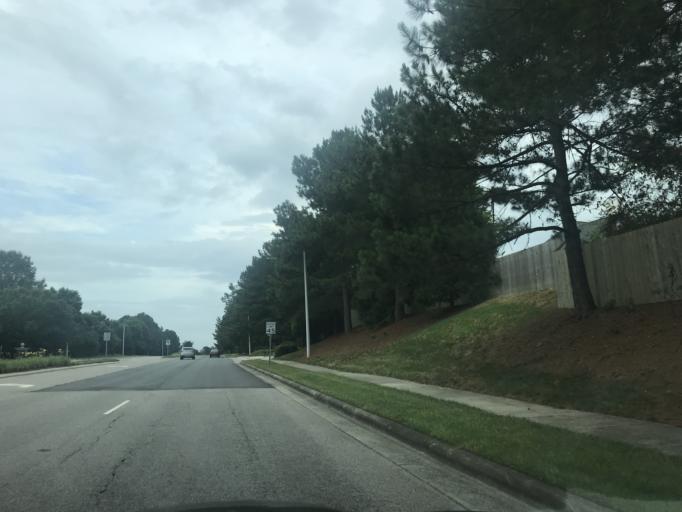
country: US
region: North Carolina
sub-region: Wake County
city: Morrisville
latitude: 35.8139
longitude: -78.8581
